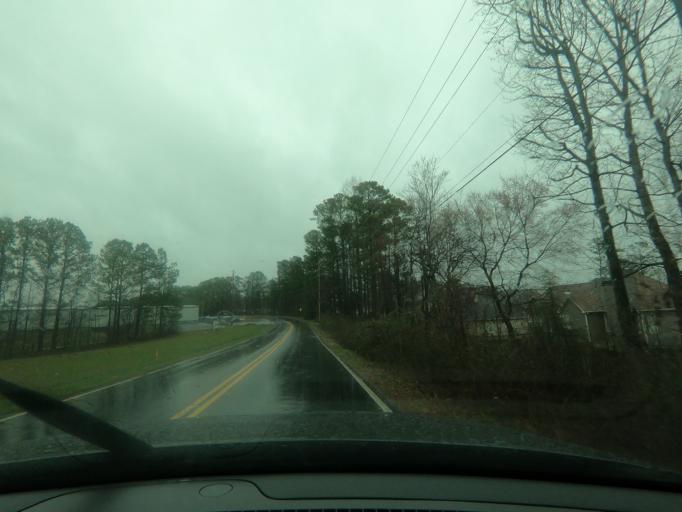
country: US
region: Georgia
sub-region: Cobb County
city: Kennesaw
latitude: 34.0560
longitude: -84.6391
